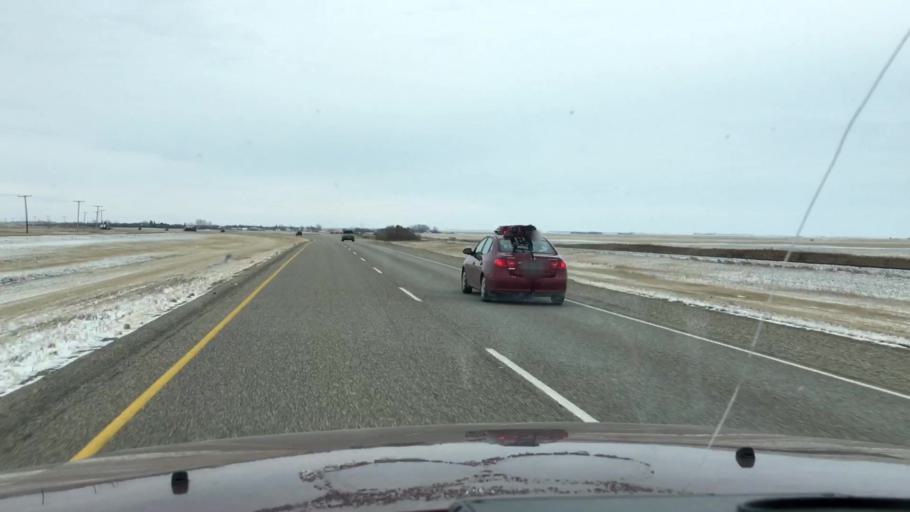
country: CA
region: Saskatchewan
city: Watrous
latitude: 51.1741
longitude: -105.9335
